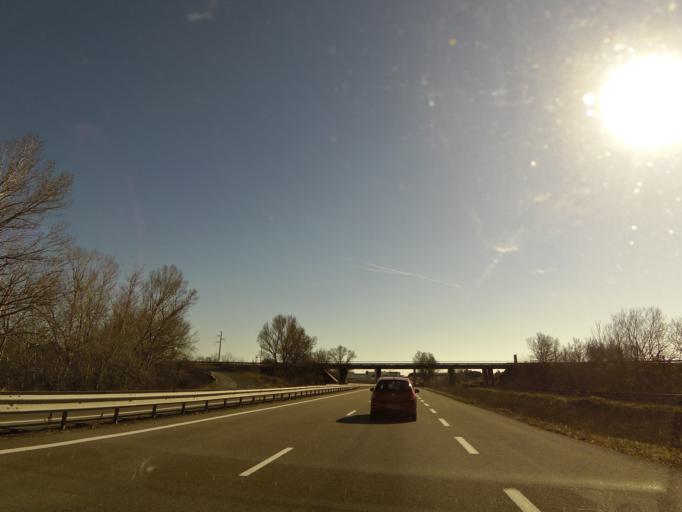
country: FR
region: Languedoc-Roussillon
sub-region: Departement du Gard
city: Aigues-Mortes
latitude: 43.5815
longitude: 4.1976
